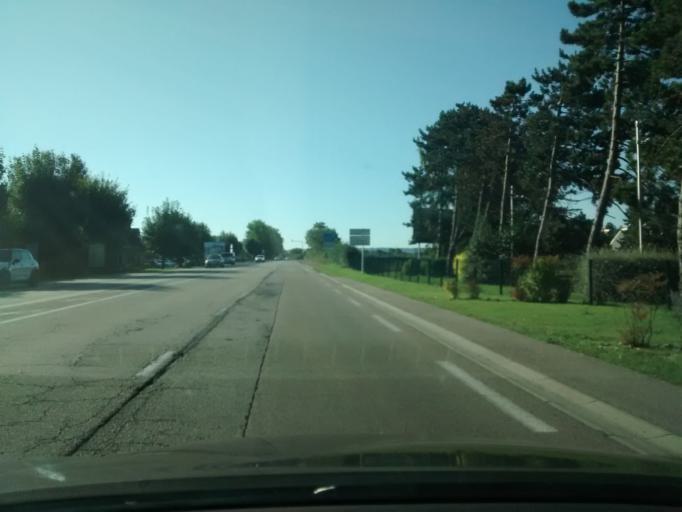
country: FR
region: Lower Normandy
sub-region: Departement du Calvados
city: Touques
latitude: 49.3421
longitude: 0.1013
